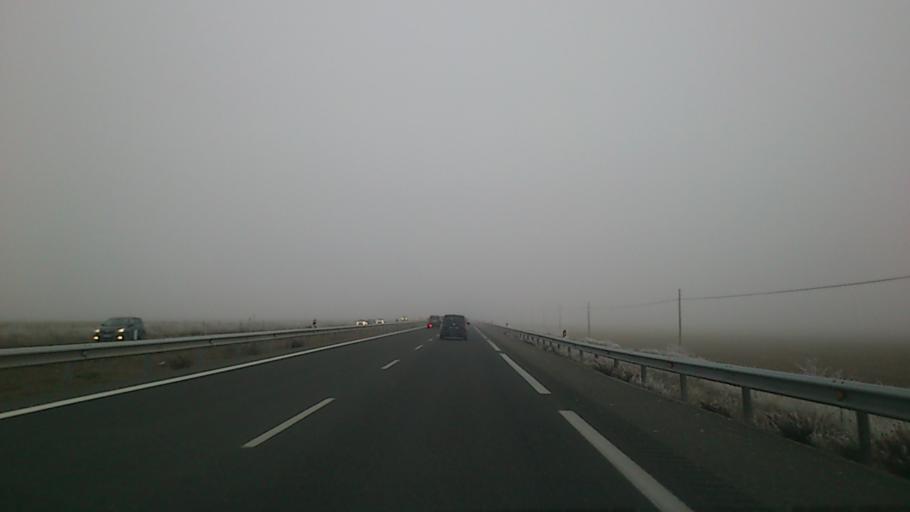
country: ES
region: Castille-La Mancha
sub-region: Provincia de Guadalajara
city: Almadrones
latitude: 40.8798
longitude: -2.7919
